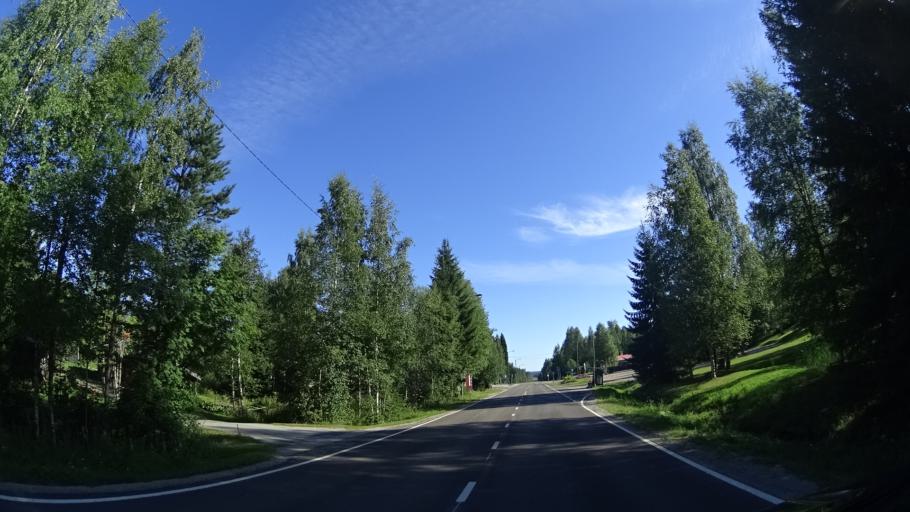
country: FI
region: Central Finland
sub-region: Jyvaeskylae
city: Uurainen
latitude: 62.4247
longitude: 25.3731
